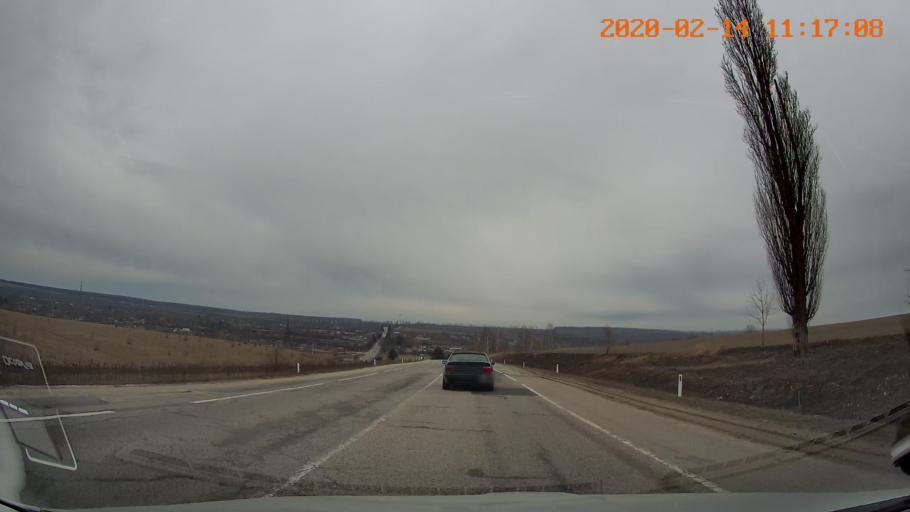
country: MD
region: Raionul Edinet
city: Edinet
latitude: 48.2580
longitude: 27.1961
